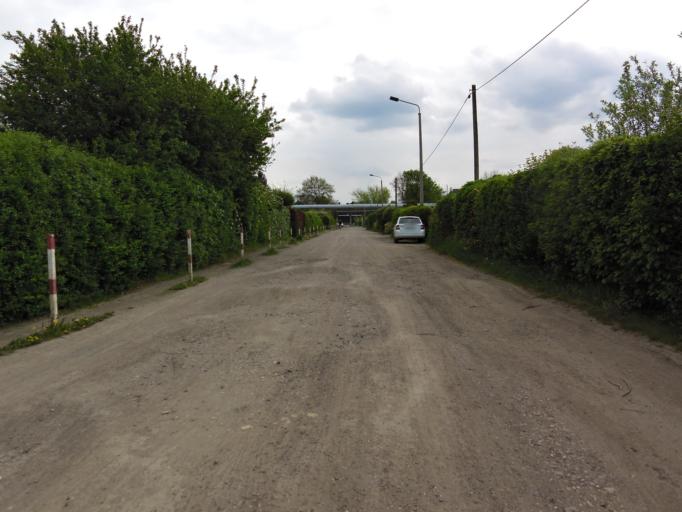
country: DE
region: Saxony
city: Markkleeberg
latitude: 51.3067
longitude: 12.3341
